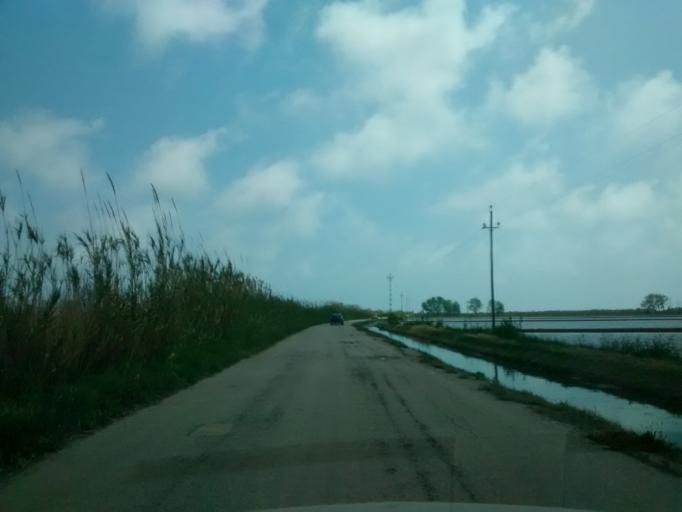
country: ES
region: Catalonia
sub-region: Provincia de Tarragona
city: Deltebre
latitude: 40.6974
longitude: 0.8344
